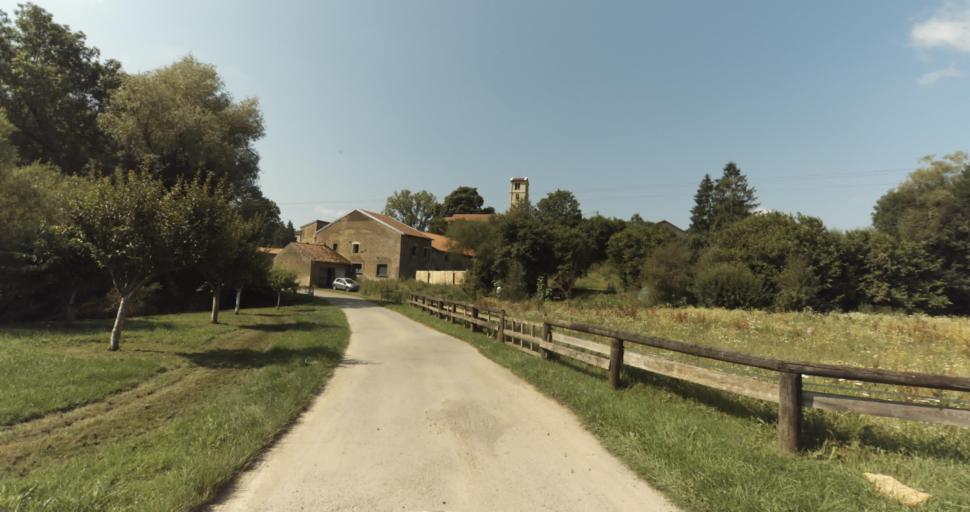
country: FR
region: Lorraine
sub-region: Departement de Meurthe-et-Moselle
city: Mancieulles
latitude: 49.2830
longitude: 5.8900
